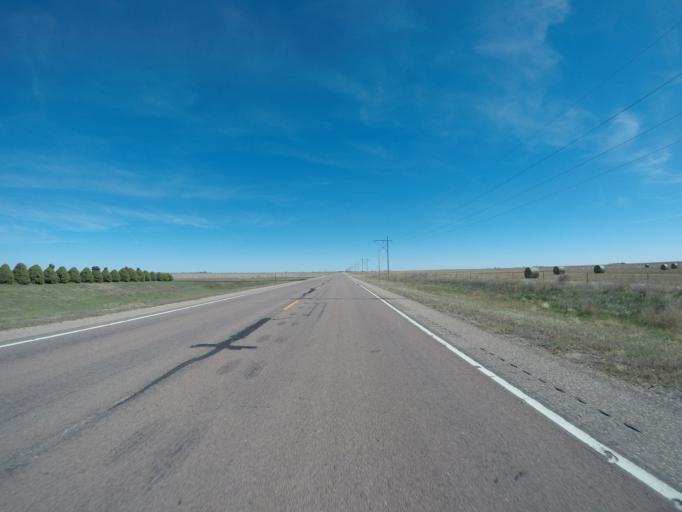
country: US
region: Colorado
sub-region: Yuma County
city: Yuma
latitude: 39.6556
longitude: -102.7464
